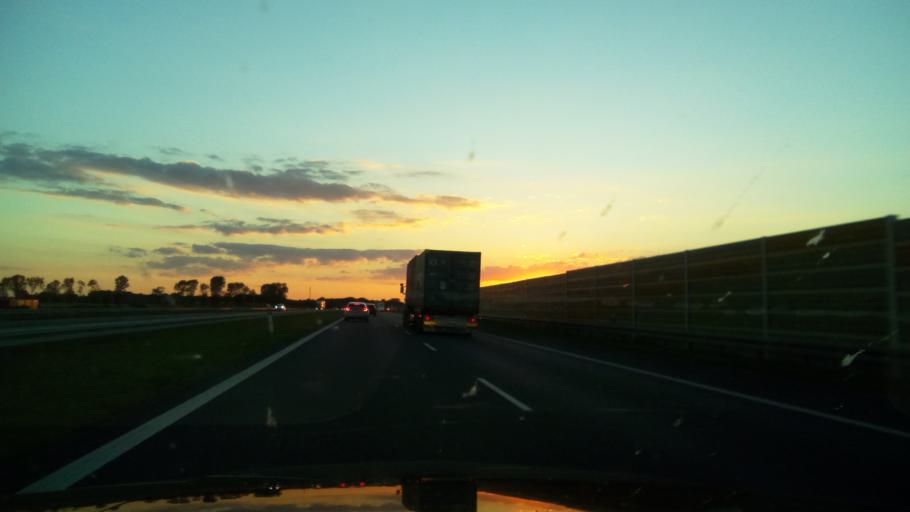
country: PL
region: Lodz Voivodeship
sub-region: Powiat poddebicki
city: Dalikow
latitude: 51.9676
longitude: 19.1038
